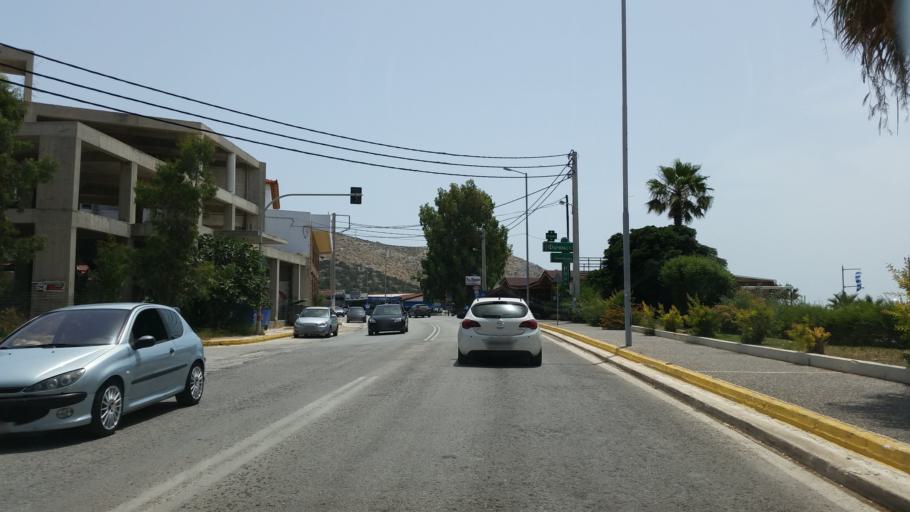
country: GR
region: Attica
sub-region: Nomarchia Anatolikis Attikis
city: Palaia Fokaia
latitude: 37.7182
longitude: 23.9461
